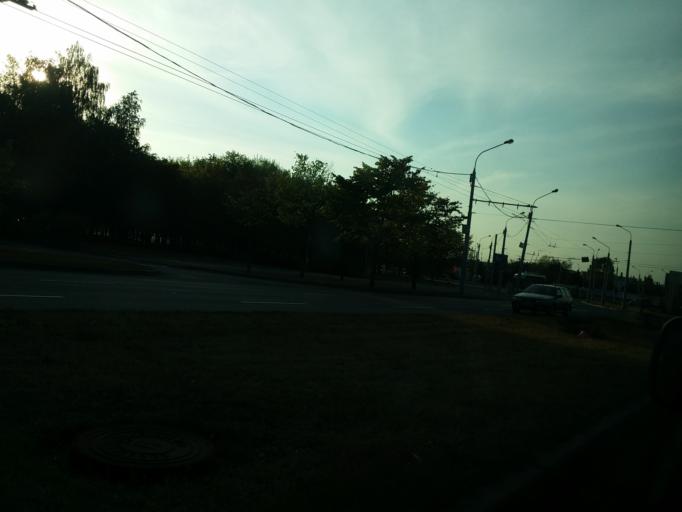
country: BY
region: Minsk
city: Minsk
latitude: 53.8931
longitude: 27.6453
